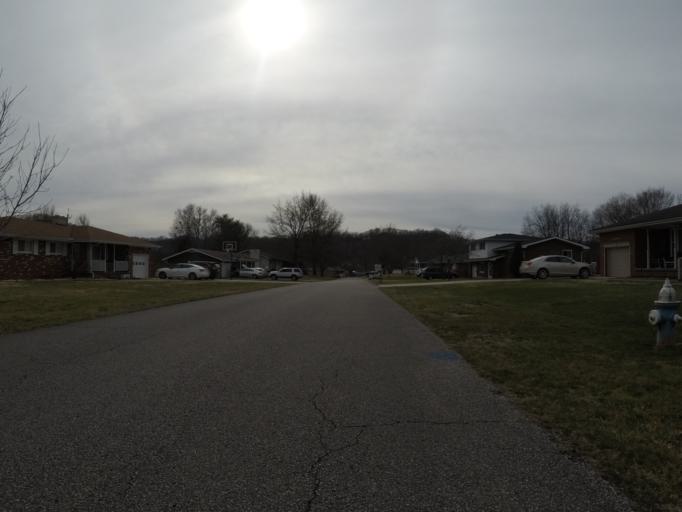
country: US
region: West Virginia
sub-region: Cabell County
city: Pea Ridge
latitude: 38.4463
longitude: -82.3392
